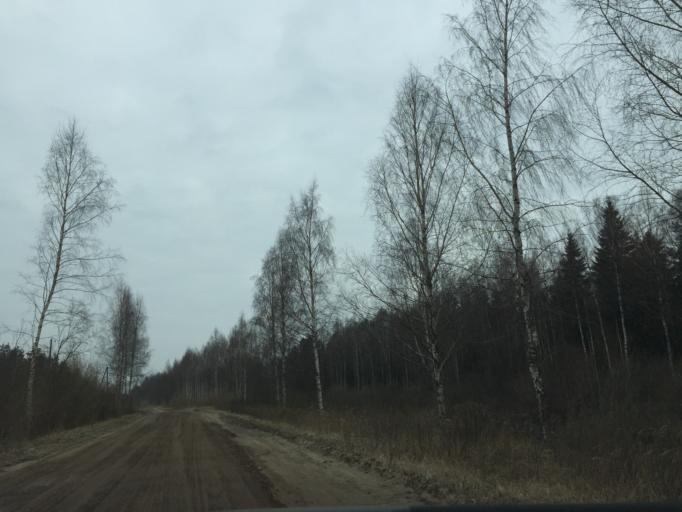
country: LV
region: Kekava
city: Balozi
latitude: 56.7891
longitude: 24.1329
